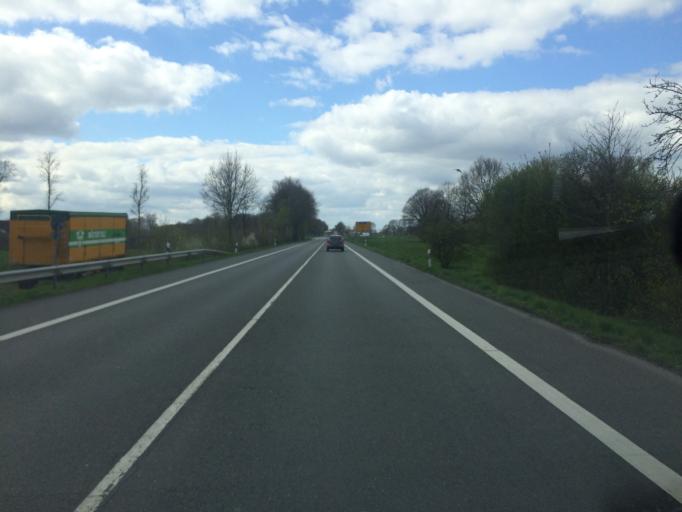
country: DE
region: North Rhine-Westphalia
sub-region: Regierungsbezirk Munster
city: Coesfeld
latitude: 51.9345
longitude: 7.1243
